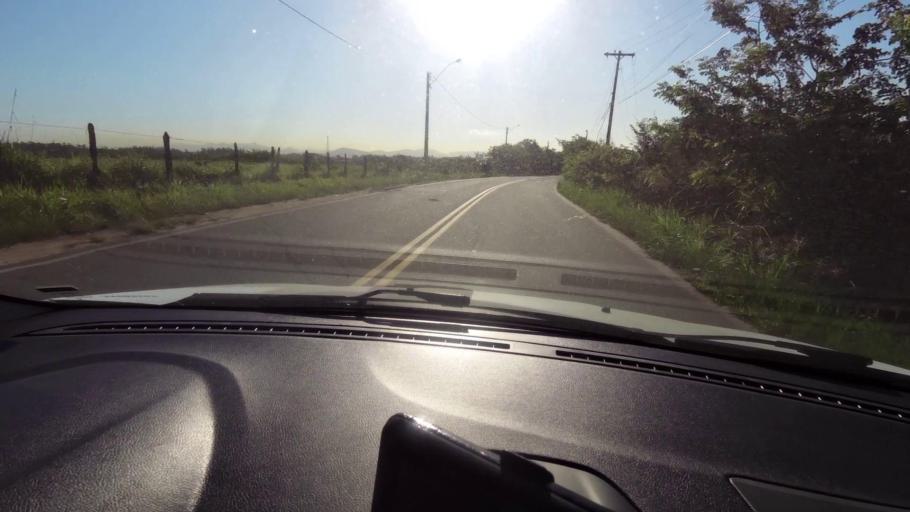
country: BR
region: Espirito Santo
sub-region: Piuma
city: Piuma
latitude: -20.7969
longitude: -40.6006
